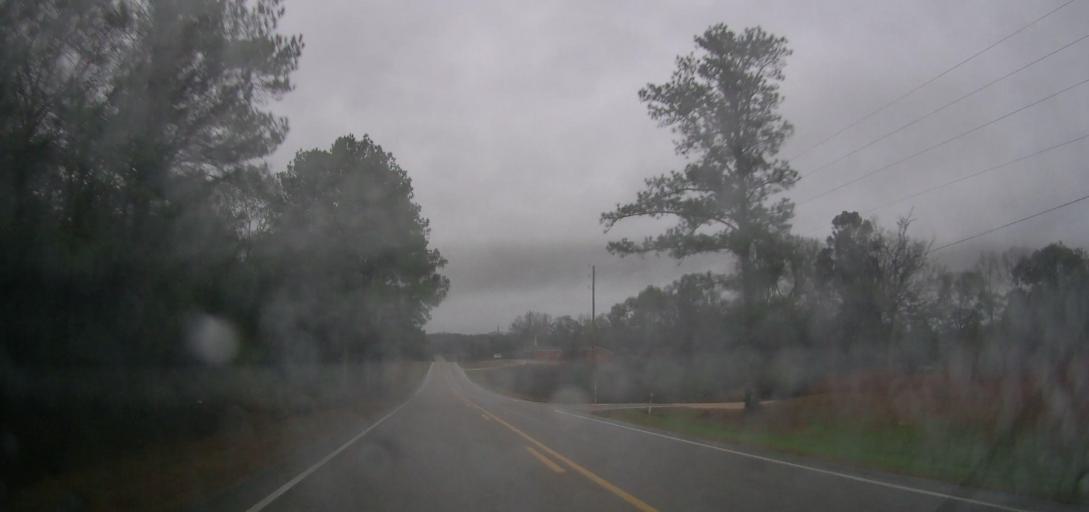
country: US
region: Alabama
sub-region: Autauga County
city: Pine Level
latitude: 32.5400
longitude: -86.6427
